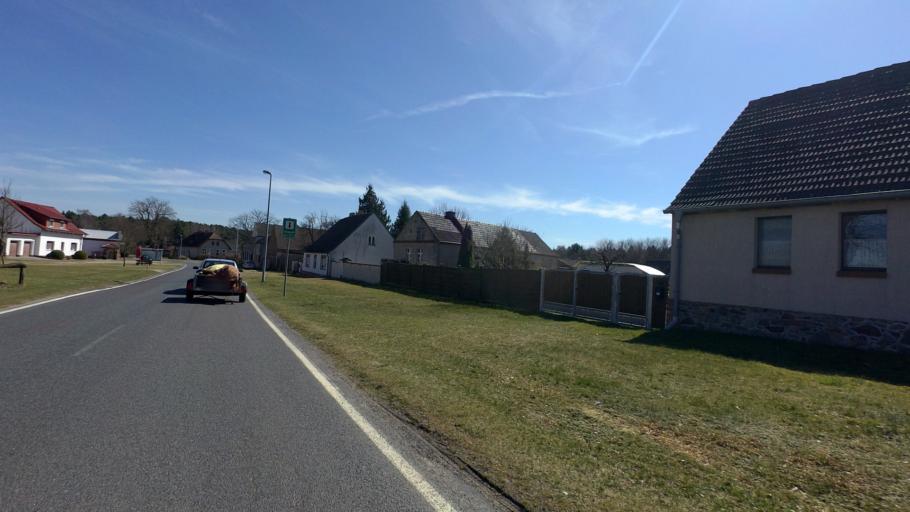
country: DE
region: Brandenburg
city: Munchehofe
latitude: 52.1595
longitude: 13.8747
